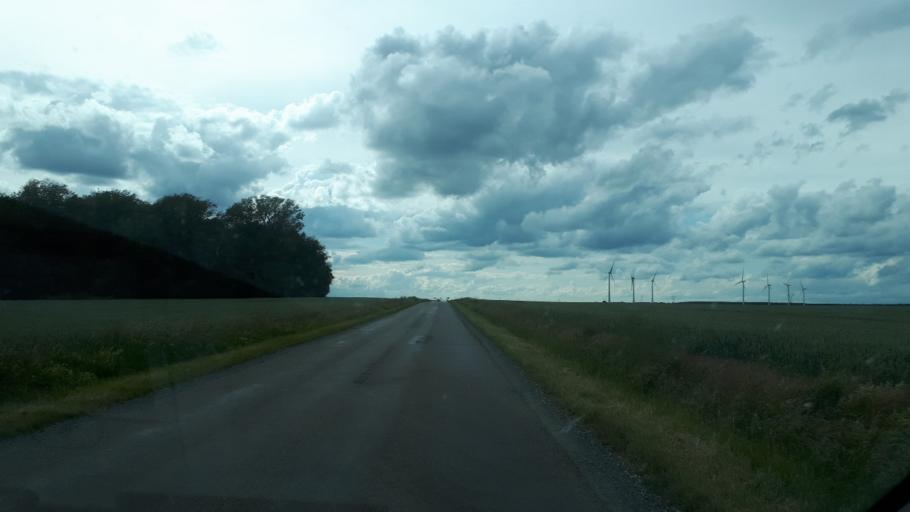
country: FR
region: Centre
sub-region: Departement du Cher
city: Massay
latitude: 47.0990
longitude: 1.9632
